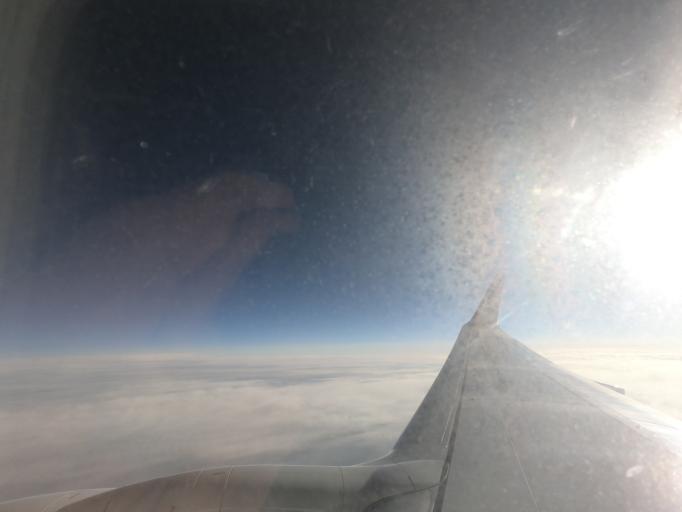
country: BE
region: Flanders
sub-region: Provincie Vlaams-Brabant
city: Tienen
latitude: 50.8366
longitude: 4.9249
